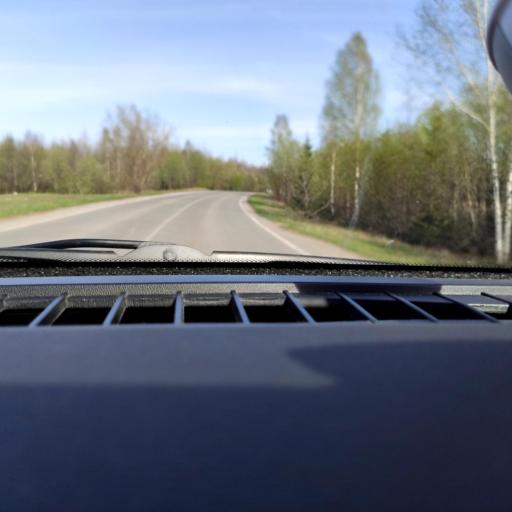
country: RU
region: Perm
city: Perm
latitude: 58.2487
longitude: 56.1394
